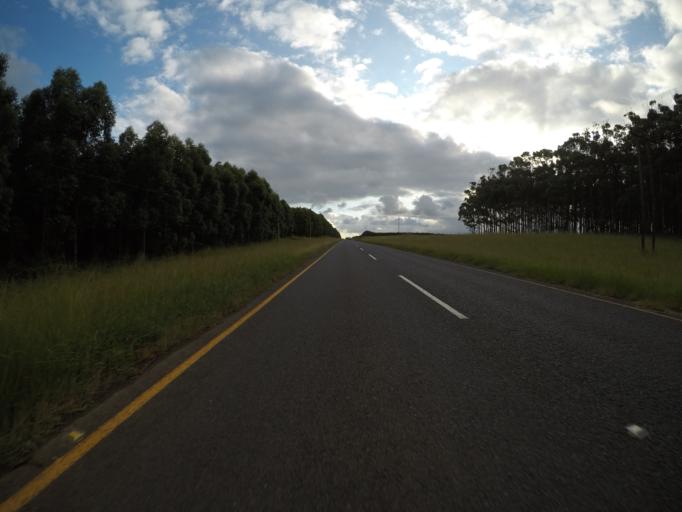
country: ZA
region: KwaZulu-Natal
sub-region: uMkhanyakude District Municipality
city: Mtubatuba
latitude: -28.3884
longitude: 32.2318
